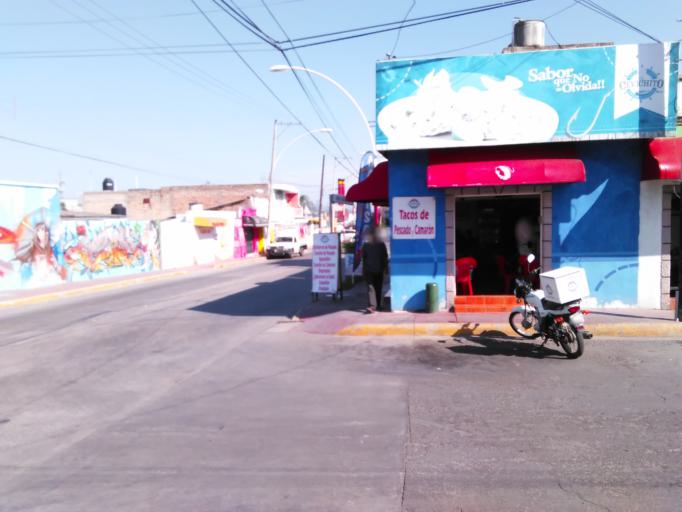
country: MX
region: Nayarit
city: Tepic
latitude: 21.4846
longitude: -104.8897
